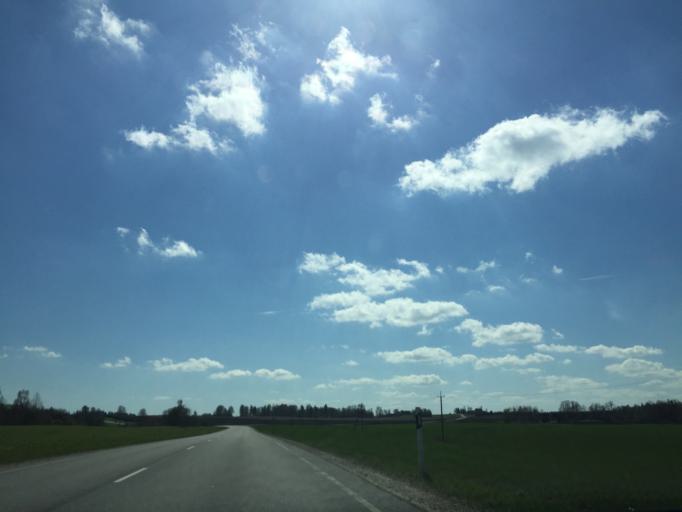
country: EE
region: Tartu
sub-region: Elva linn
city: Elva
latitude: 58.1213
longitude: 26.2416
